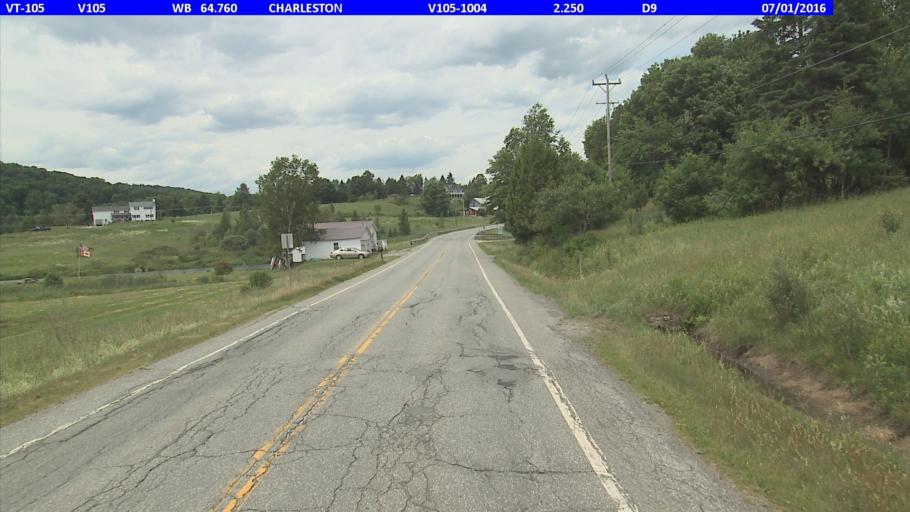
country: US
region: Vermont
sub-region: Orleans County
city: Newport
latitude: 44.8832
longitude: -72.0542
